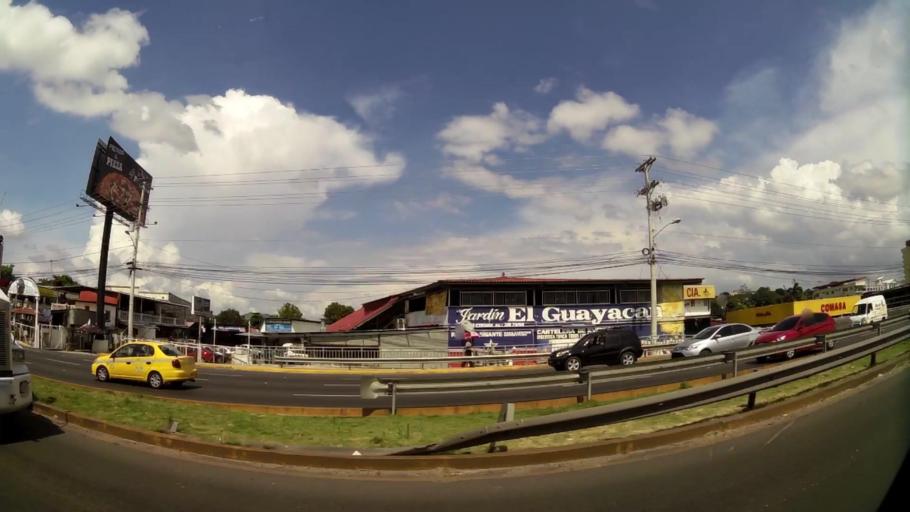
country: PA
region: Panama
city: San Miguelito
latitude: 9.0351
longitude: -79.4847
